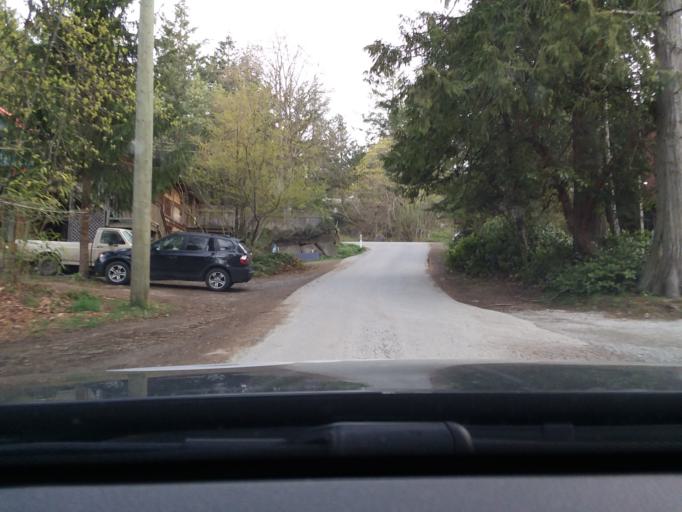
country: CA
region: British Columbia
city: North Saanich
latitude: 48.8789
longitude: -123.3203
